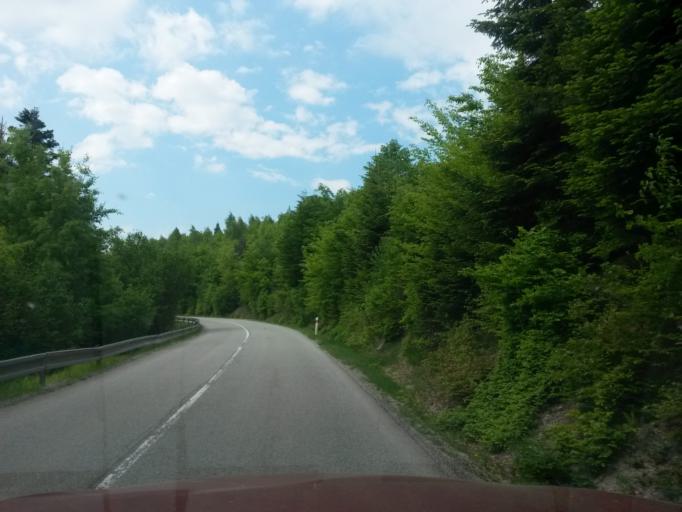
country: SK
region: Kosicky
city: Medzev
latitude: 48.7248
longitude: 20.7683
